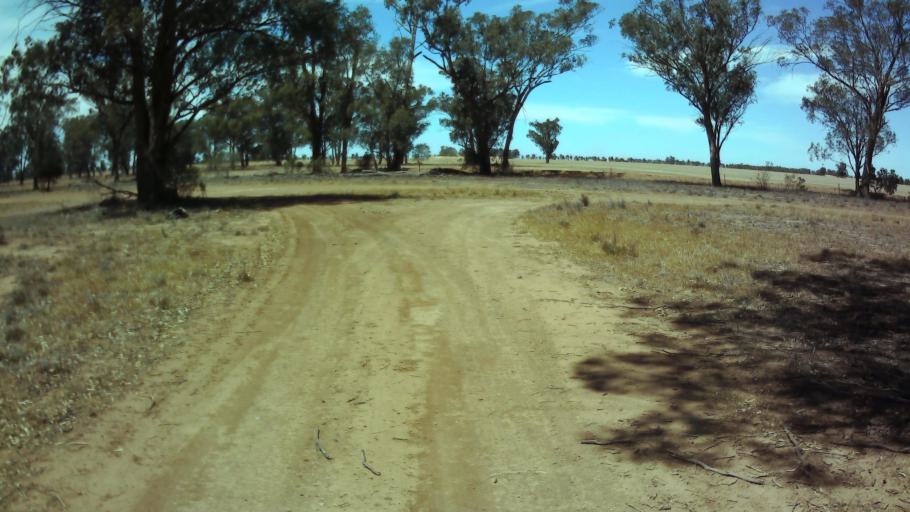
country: AU
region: New South Wales
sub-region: Weddin
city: Grenfell
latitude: -33.9329
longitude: 147.8025
